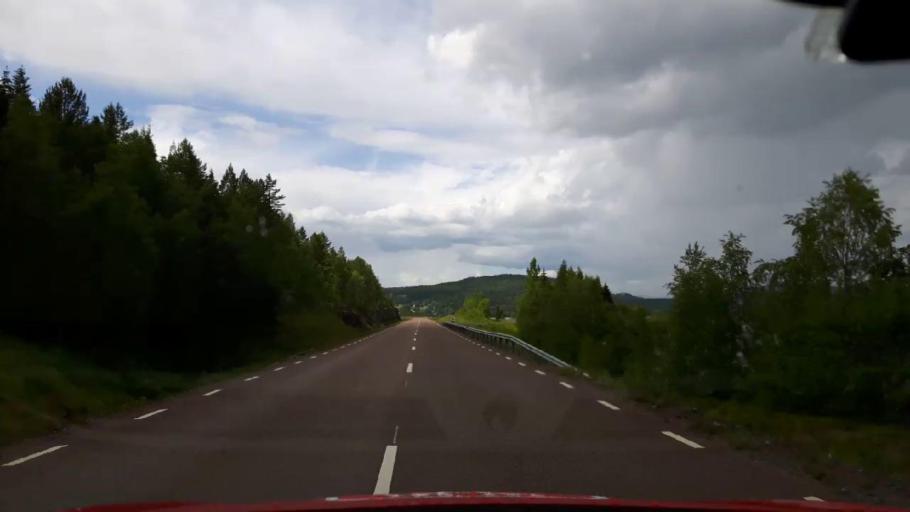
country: SE
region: Jaemtland
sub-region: Krokoms Kommun
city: Valla
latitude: 63.8968
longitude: 14.2521
